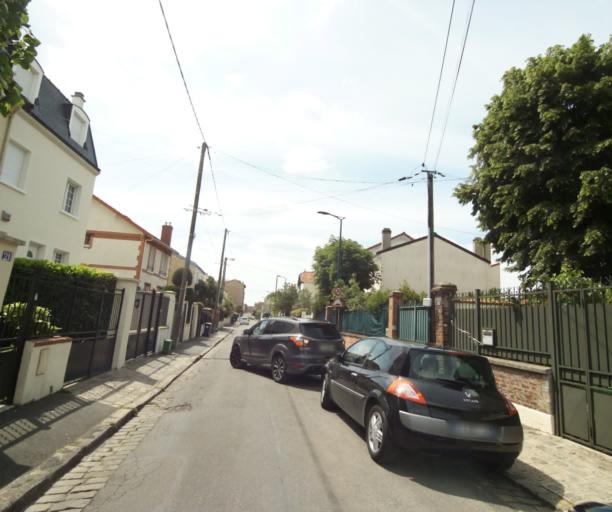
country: FR
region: Ile-de-France
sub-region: Departement des Hauts-de-Seine
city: La Garenne-Colombes
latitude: 48.9150
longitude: 2.2411
